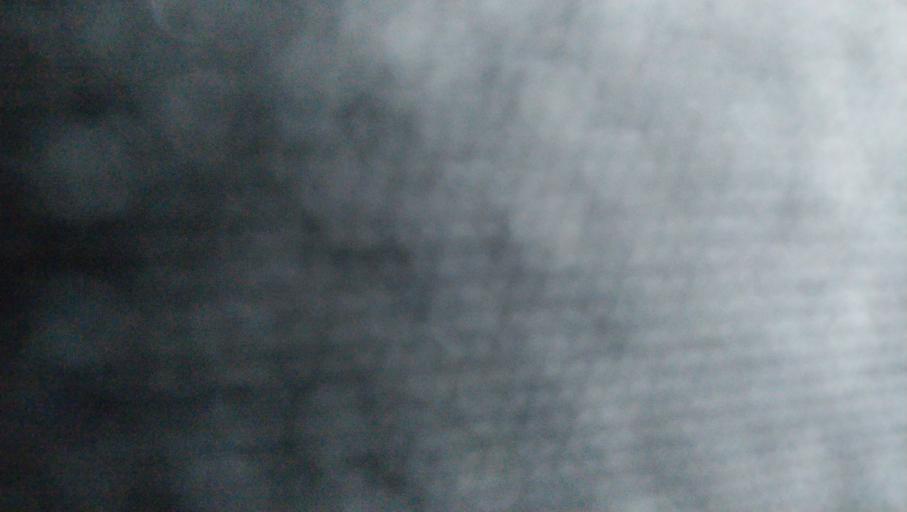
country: MX
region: Oaxaca
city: Juchitan de Zaragoza
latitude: 16.4474
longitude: -95.0231
